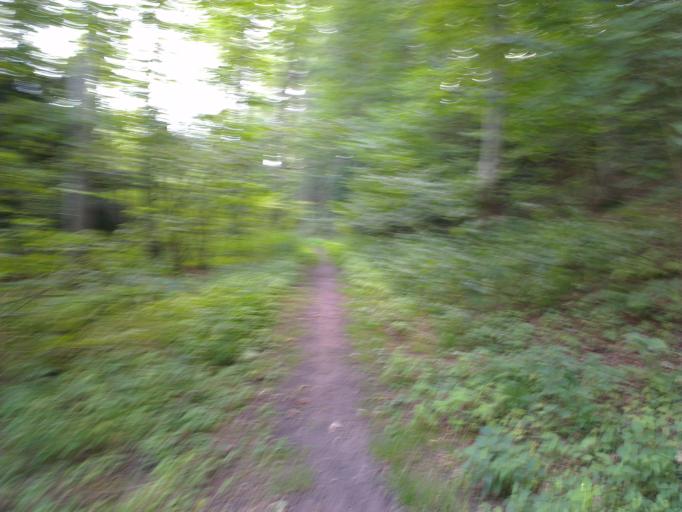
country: DK
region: Capital Region
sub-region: Frederikssund Kommune
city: Frederikssund
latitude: 55.8500
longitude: 12.0276
